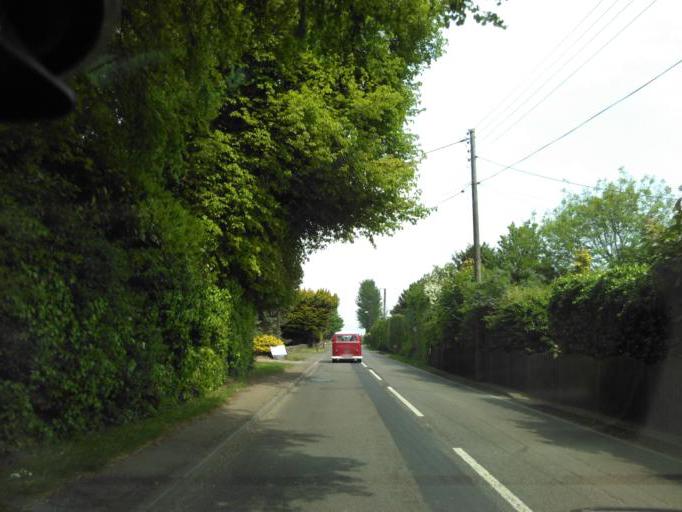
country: GB
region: England
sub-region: Kent
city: Chartham
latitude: 51.2177
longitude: 1.0604
